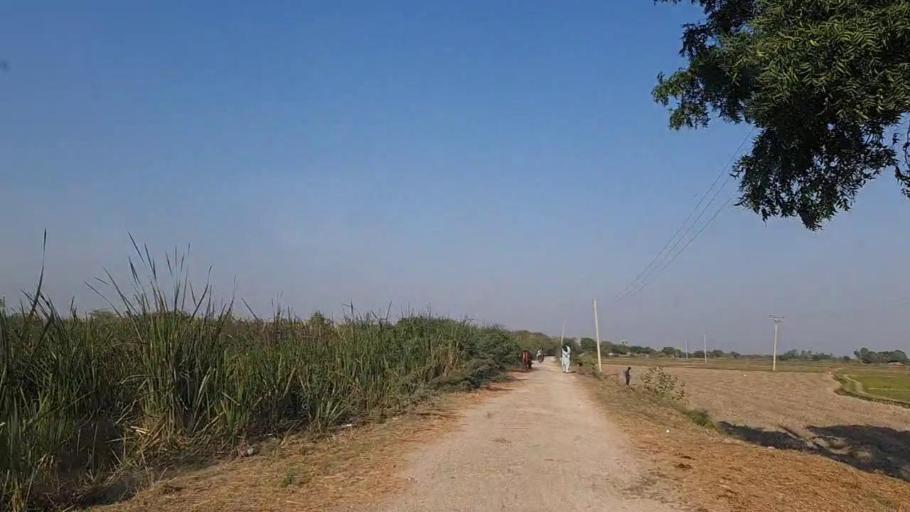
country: PK
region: Sindh
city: Thatta
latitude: 24.7188
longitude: 67.9430
